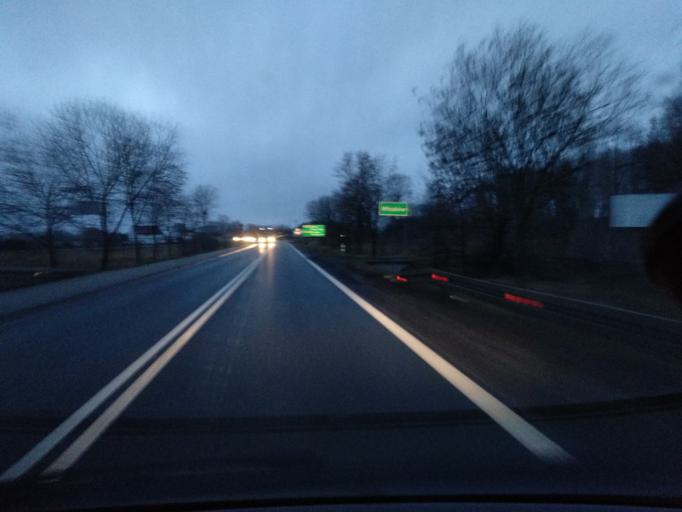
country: PL
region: Lower Silesian Voivodeship
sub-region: Powiat sredzki
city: Malczyce
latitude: 51.1932
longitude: 16.5045
